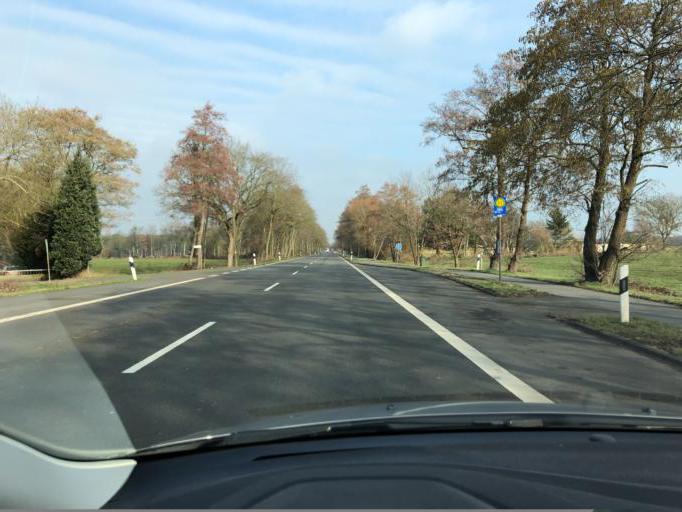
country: DE
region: Lower Saxony
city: Hesel
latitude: 53.3216
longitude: 7.5998
